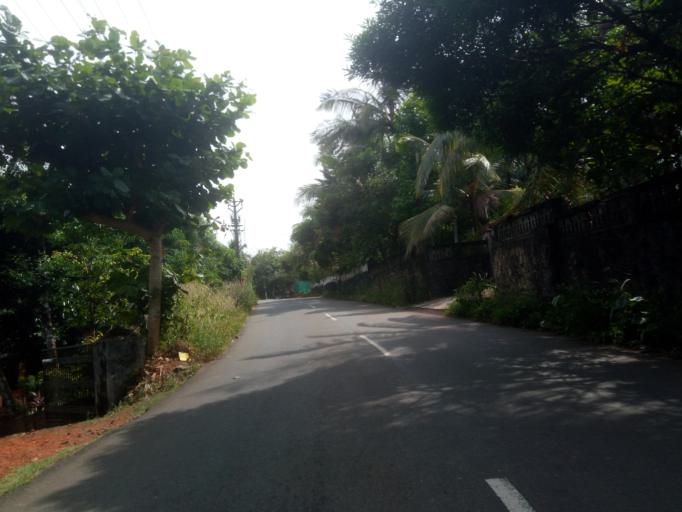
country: IN
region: Kerala
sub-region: Malappuram
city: Ponnani
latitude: 10.8170
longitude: 76.0264
